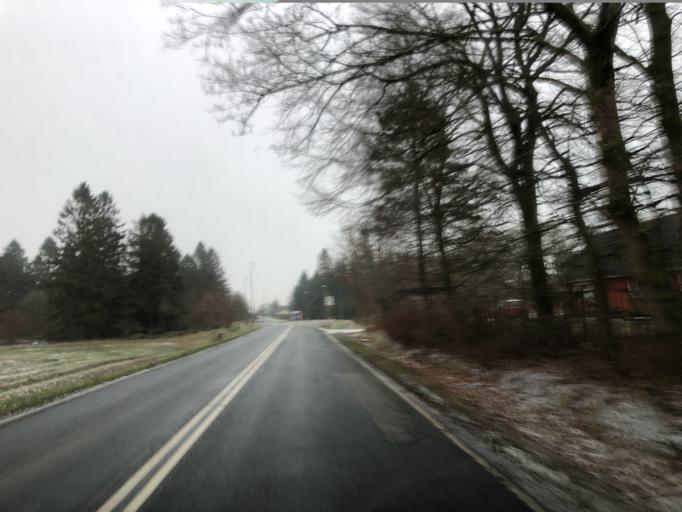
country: DK
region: South Denmark
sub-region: Vejle Kommune
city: Give
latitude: 55.8319
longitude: 9.3126
